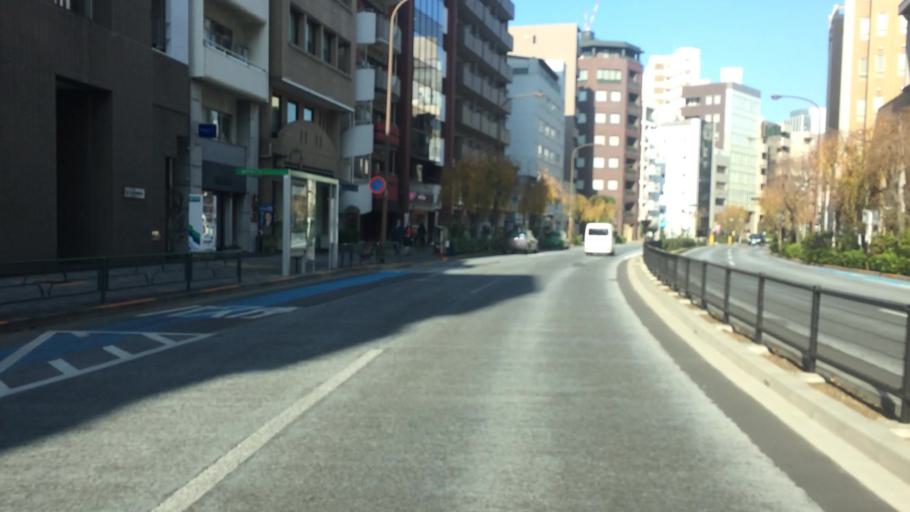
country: JP
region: Tokyo
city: Tokyo
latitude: 35.6504
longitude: 139.7098
